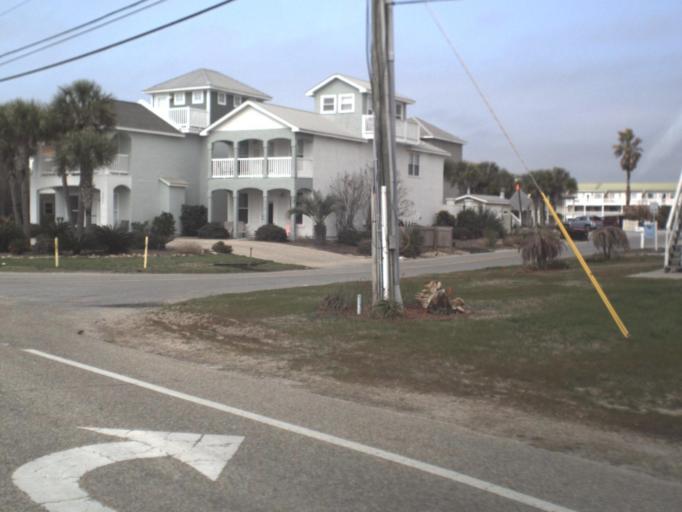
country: US
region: Florida
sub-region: Bay County
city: Laguna Beach
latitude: 30.2575
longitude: -85.9651
